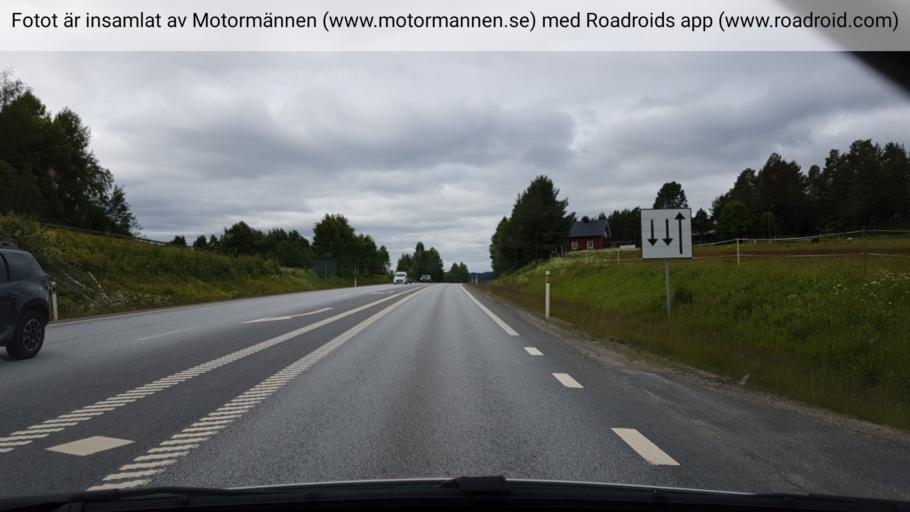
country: SE
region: Vaesterbotten
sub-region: Vannas Kommun
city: Vannasby
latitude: 63.9209
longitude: 19.8013
